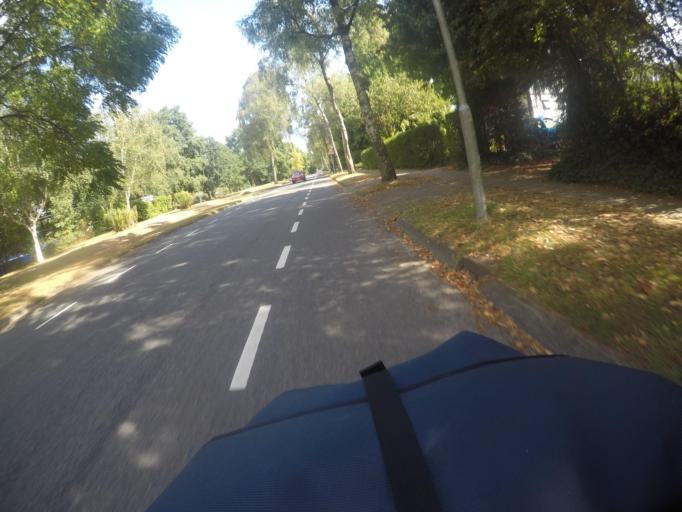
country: NL
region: Gelderland
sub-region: Gemeente Renkum
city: Oosterbeek
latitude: 51.9956
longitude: 5.8374
